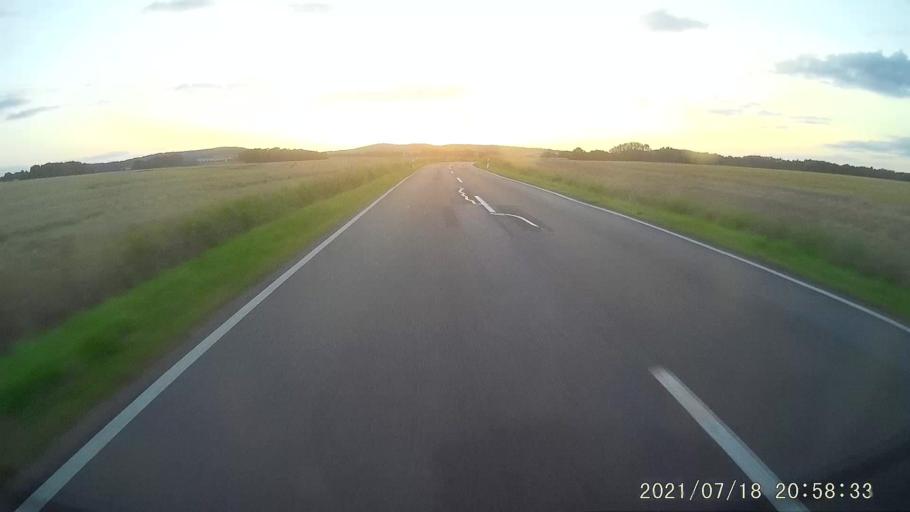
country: DE
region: Saxony
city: Markersdorf
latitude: 51.1705
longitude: 14.9124
